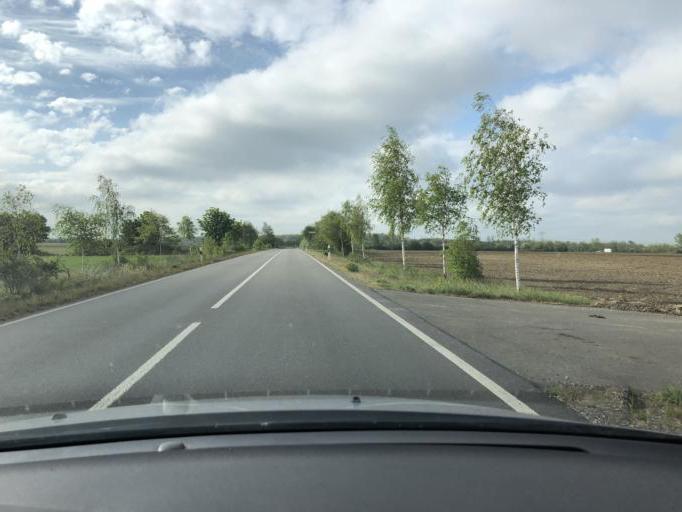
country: DE
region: Saxony
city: Neukieritzsch
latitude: 51.1608
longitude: 12.4198
